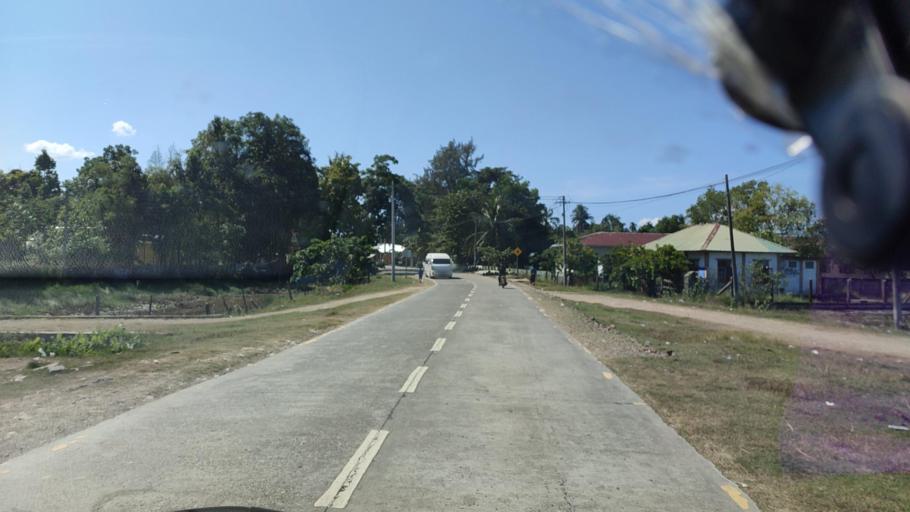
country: MM
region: Rakhine
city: Sittwe
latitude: 20.2945
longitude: 92.8830
